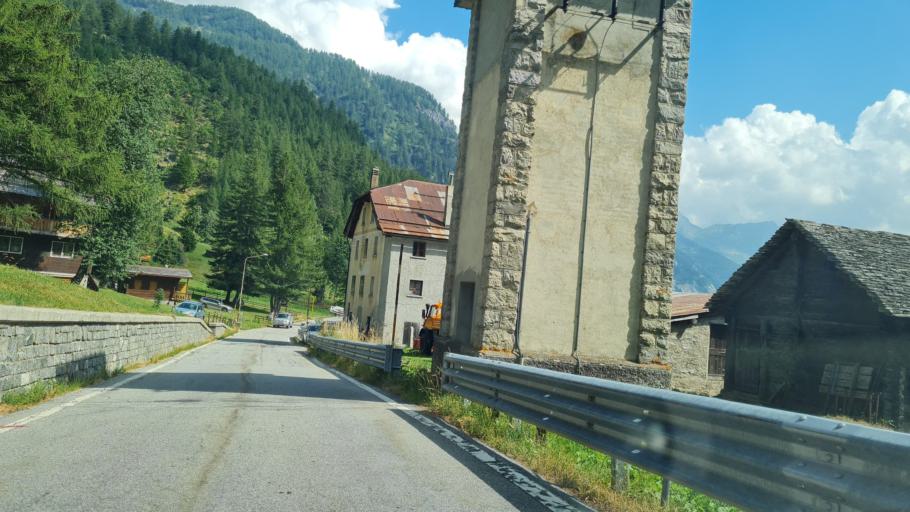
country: IT
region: Piedmont
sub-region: Provincia Verbano-Cusio-Ossola
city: Formazza
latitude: 46.3931
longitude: 8.4199
